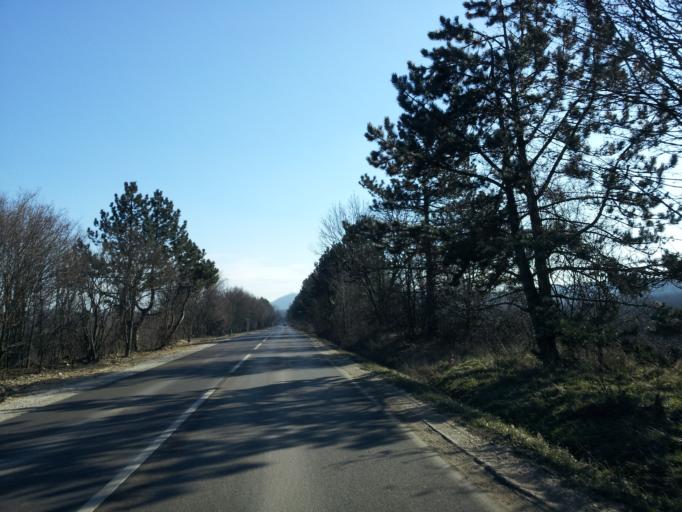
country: HU
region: Pest
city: Solymar
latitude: 47.5542
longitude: 18.9280
